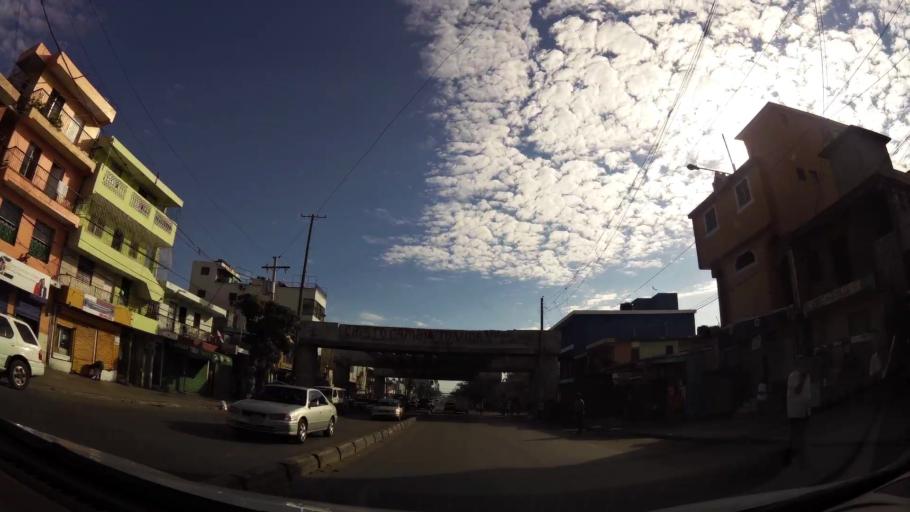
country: DO
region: Nacional
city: Ensanche Luperon
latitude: 18.5006
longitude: -69.8889
